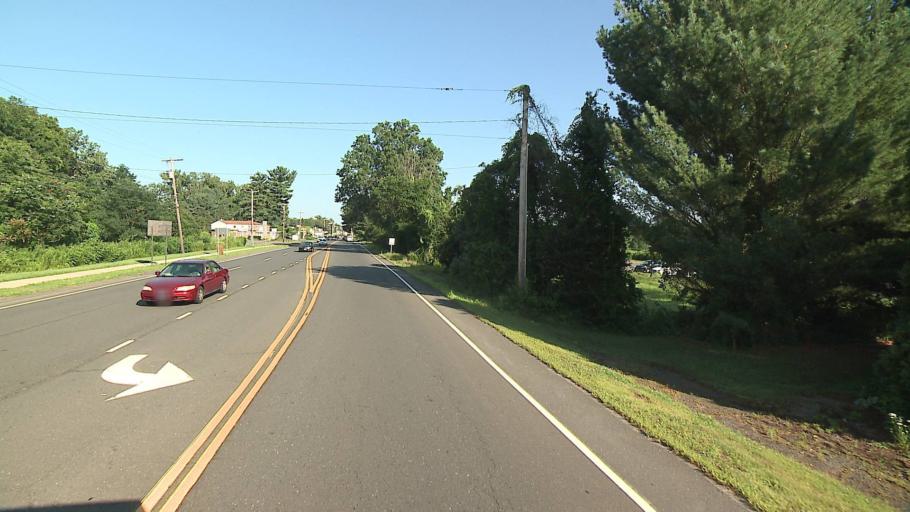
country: US
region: Connecticut
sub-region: Hartford County
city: Farmington
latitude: 41.7322
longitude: -72.8328
